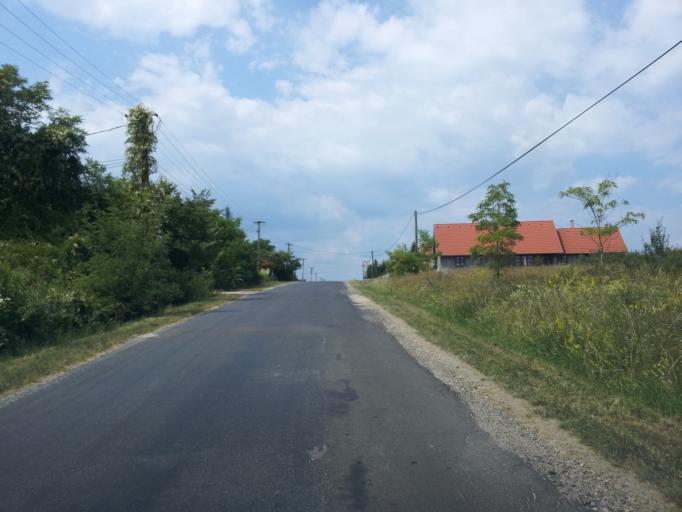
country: HU
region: Veszprem
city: Zanka
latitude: 46.9404
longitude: 17.6998
